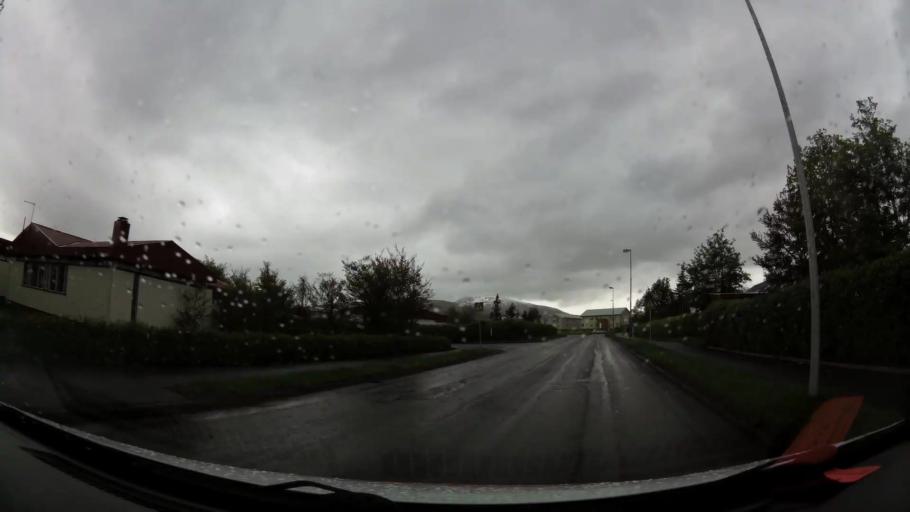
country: IS
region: Northeast
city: Akureyri
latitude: 65.6888
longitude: -18.1354
